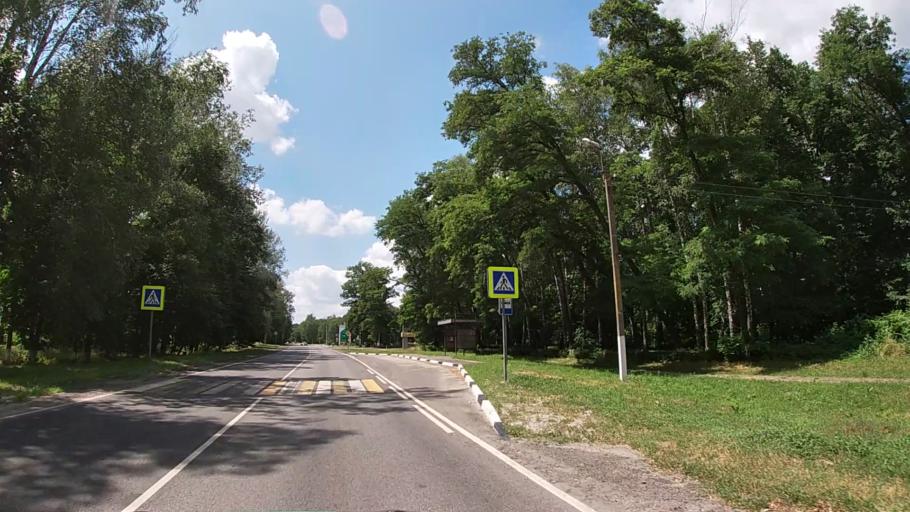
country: RU
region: Belgorod
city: Grayvoron
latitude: 50.4915
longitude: 35.6993
